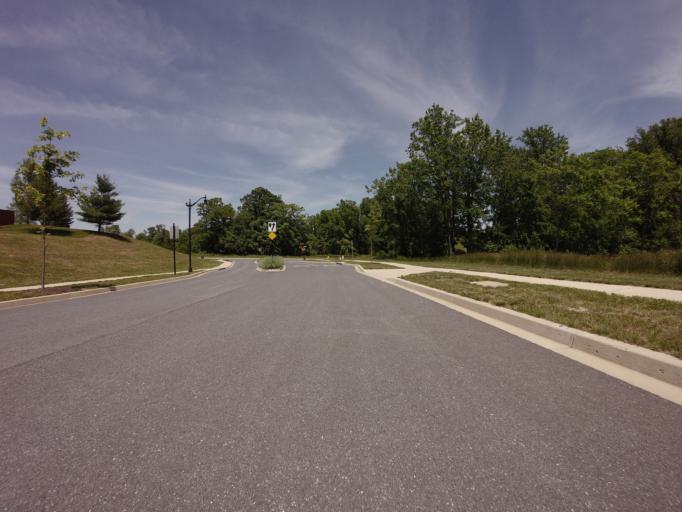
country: US
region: Maryland
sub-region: Frederick County
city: Urbana
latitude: 39.3197
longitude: -77.3469
